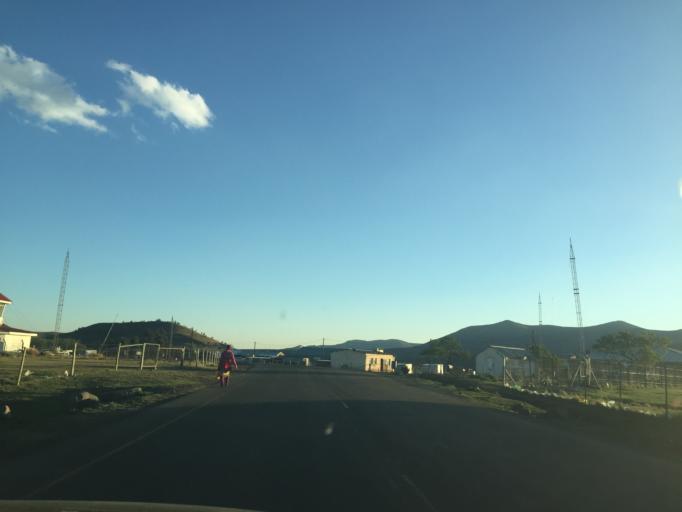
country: LS
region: Maseru
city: Nako
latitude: -29.8399
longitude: 28.0532
